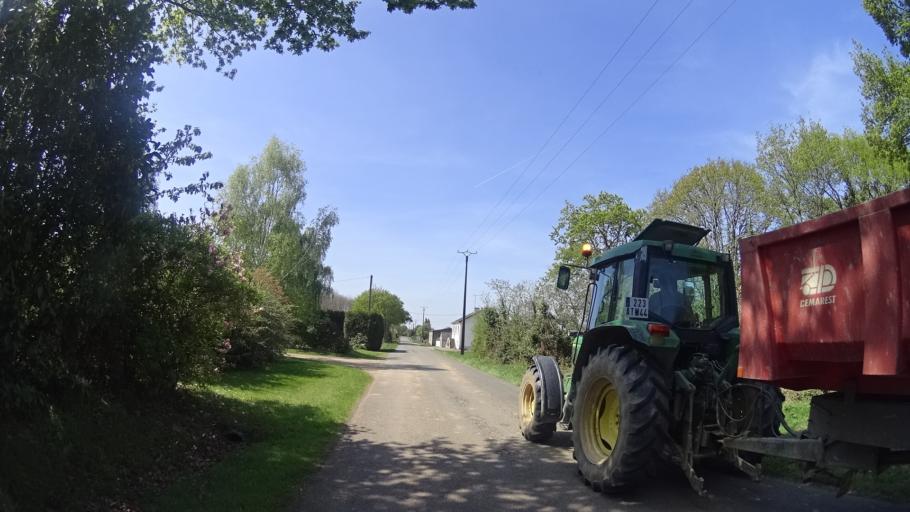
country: FR
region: Pays de la Loire
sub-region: Departement de la Loire-Atlantique
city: Fegreac
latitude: 47.5959
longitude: -2.0645
